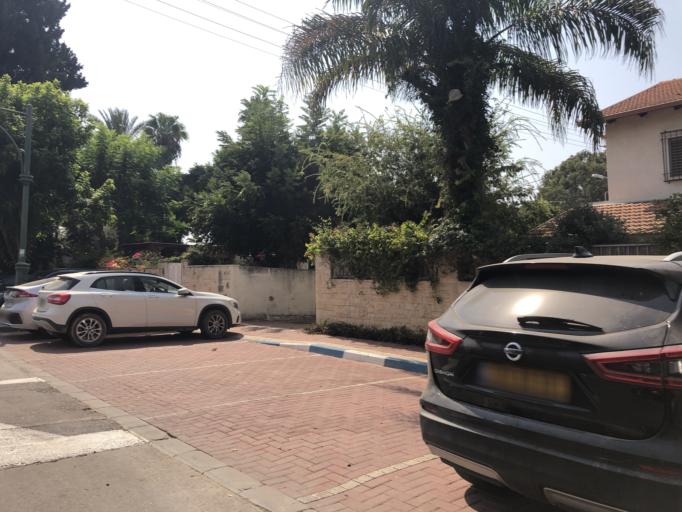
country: IL
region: Tel Aviv
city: Giv`atayim
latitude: 32.0539
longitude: 34.8316
